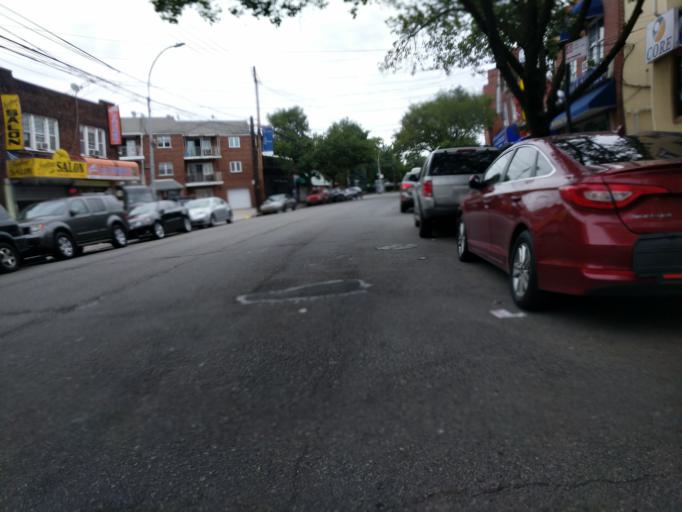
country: US
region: New York
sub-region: Queens County
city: Borough of Queens
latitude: 40.7439
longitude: -73.8569
